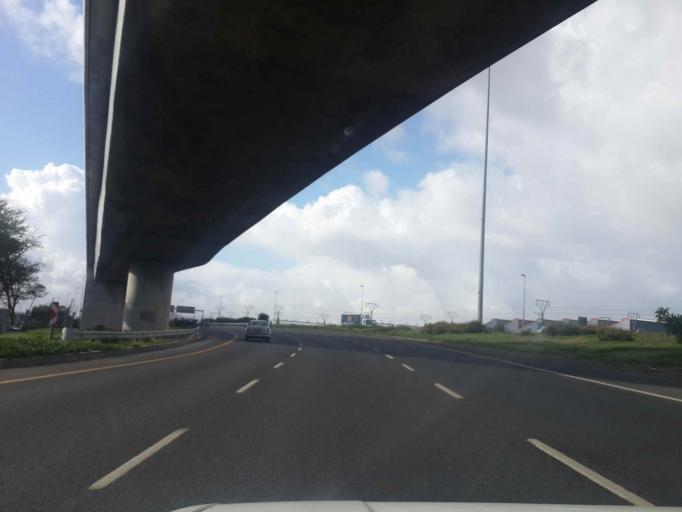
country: ZA
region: Western Cape
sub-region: City of Cape Town
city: Rosebank
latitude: -33.9169
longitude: 18.4833
